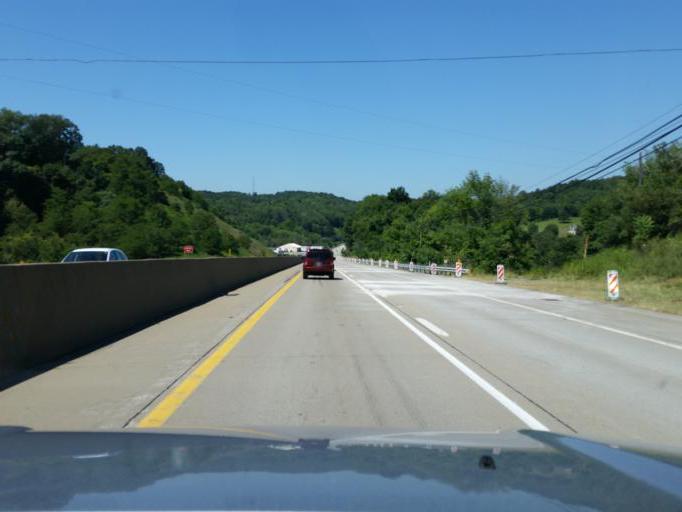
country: US
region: Pennsylvania
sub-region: Westmoreland County
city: Delmont
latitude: 40.3975
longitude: -79.4736
